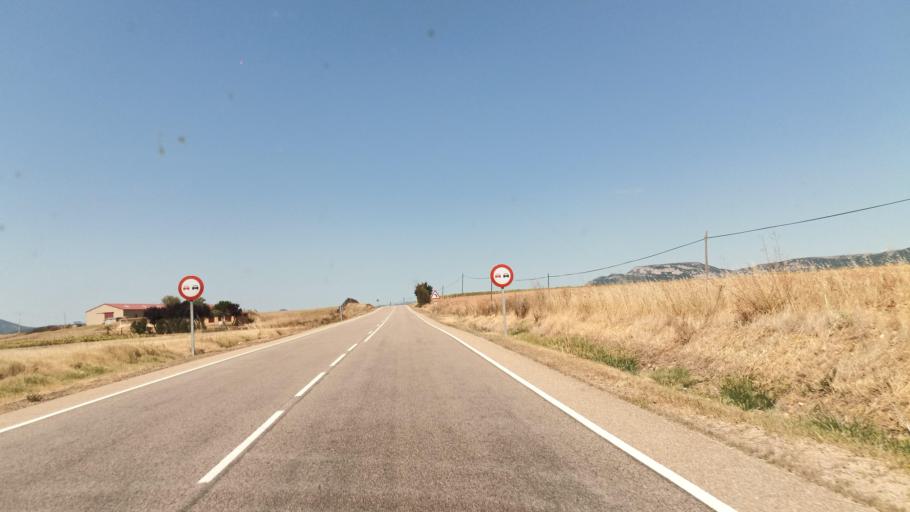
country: ES
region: Castille and Leon
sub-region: Provincia de Burgos
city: Quintanabureba
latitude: 42.6281
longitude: -3.3744
